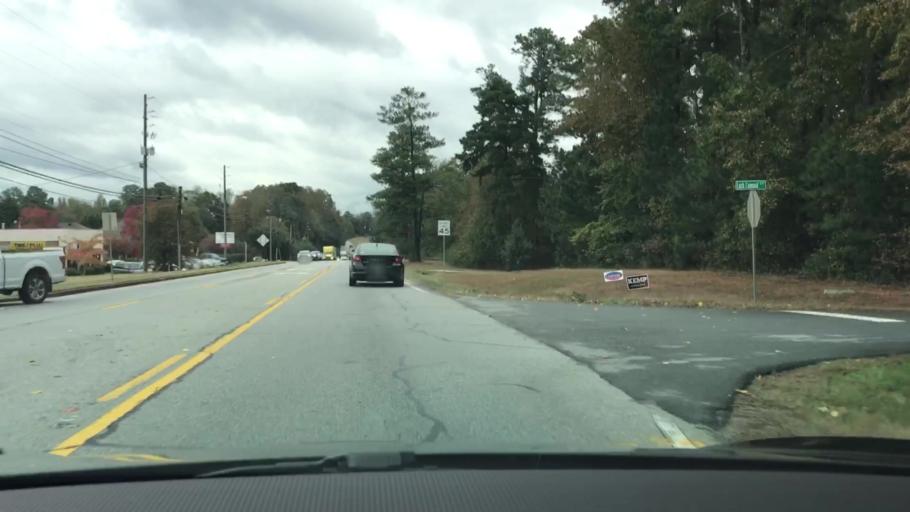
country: US
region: Georgia
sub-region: Oconee County
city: Watkinsville
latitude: 33.8724
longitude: -83.4381
